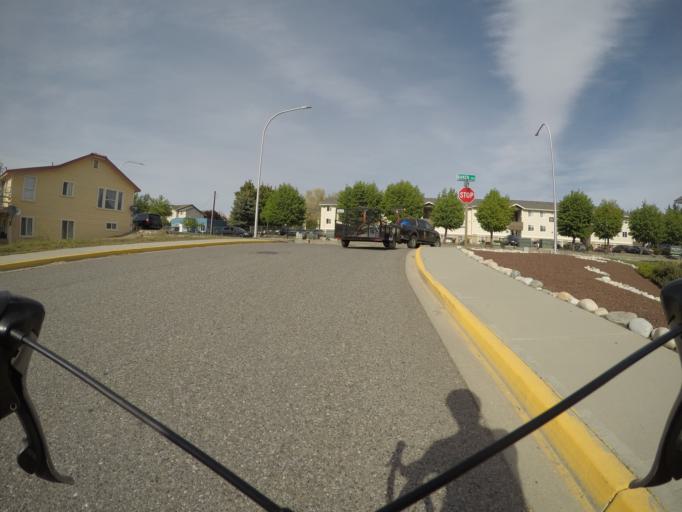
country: US
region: Washington
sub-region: Douglas County
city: East Wenatchee
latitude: 47.4143
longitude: -120.2900
